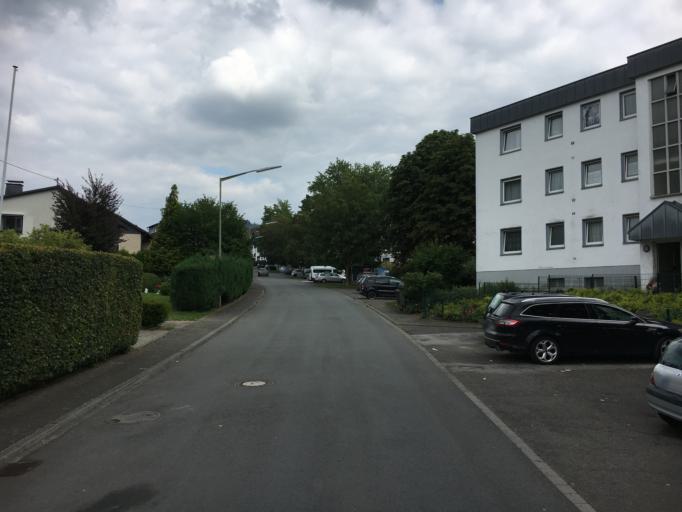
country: DE
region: North Rhine-Westphalia
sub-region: Regierungsbezirk Arnsberg
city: Lennestadt
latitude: 51.1208
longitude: 8.0544
